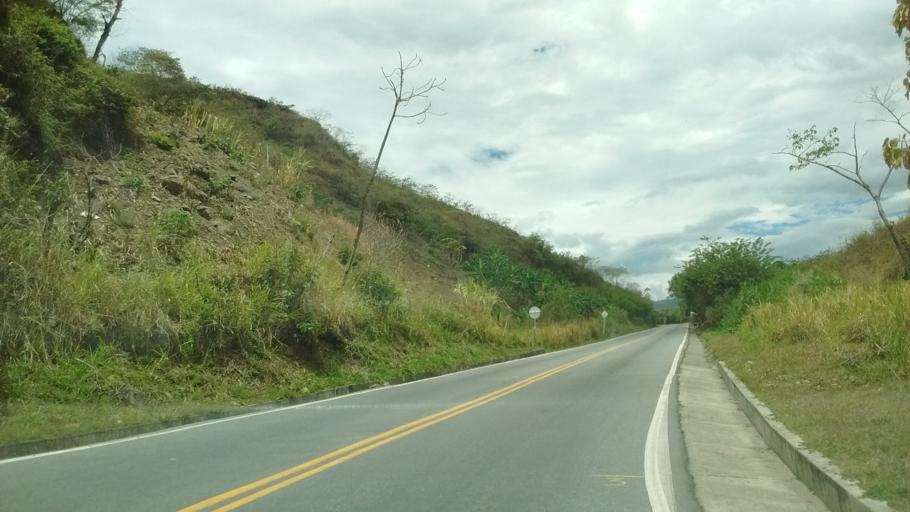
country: CO
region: Cauca
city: La Sierra
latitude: 2.2116
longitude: -76.7995
